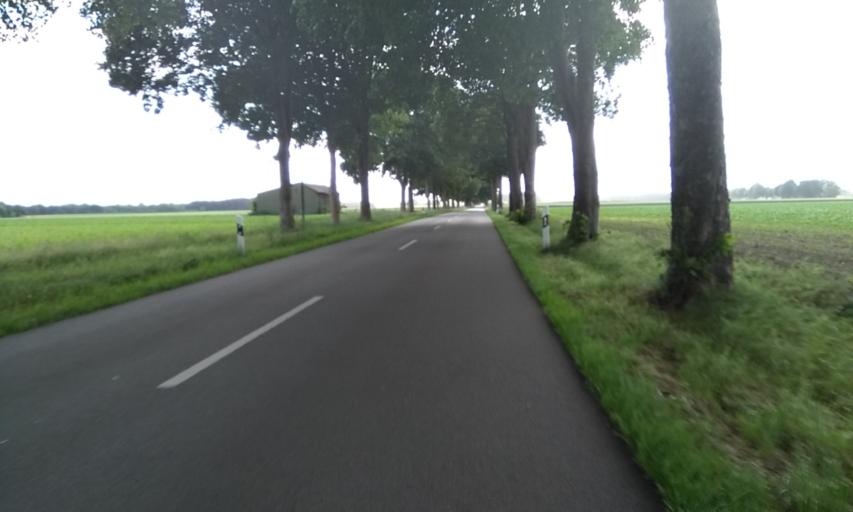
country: DE
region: Lower Saxony
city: Wohnste
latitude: 53.3563
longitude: 9.5155
